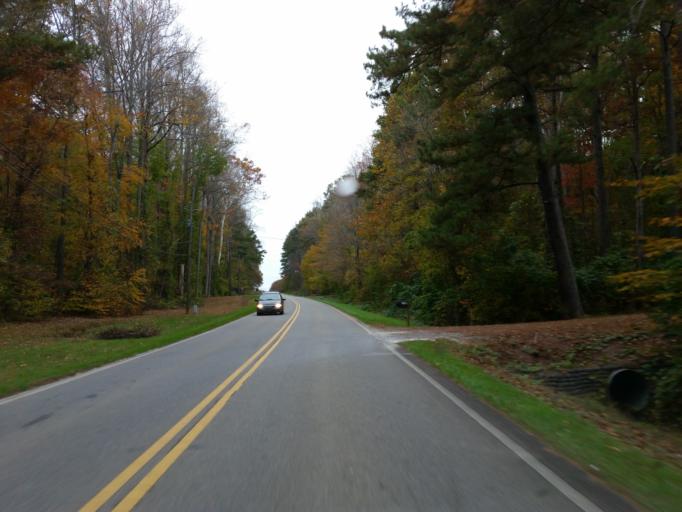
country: US
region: Georgia
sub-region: Pickens County
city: Jasper
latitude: 34.5006
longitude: -84.4346
